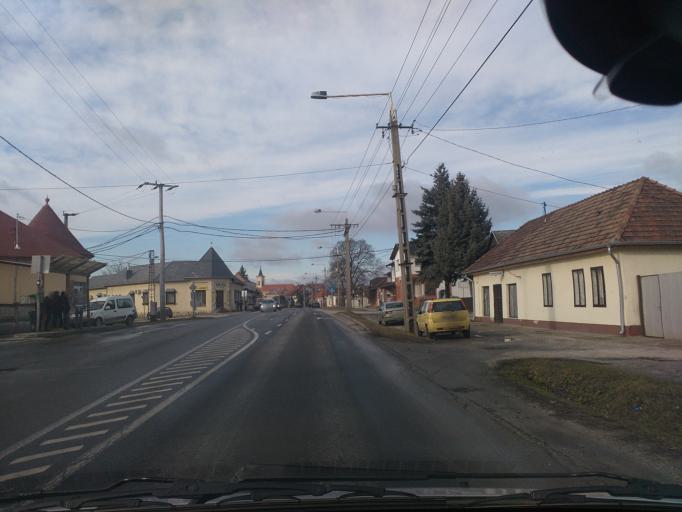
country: HU
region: Komarom-Esztergom
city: Tat
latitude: 47.7425
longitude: 18.6489
